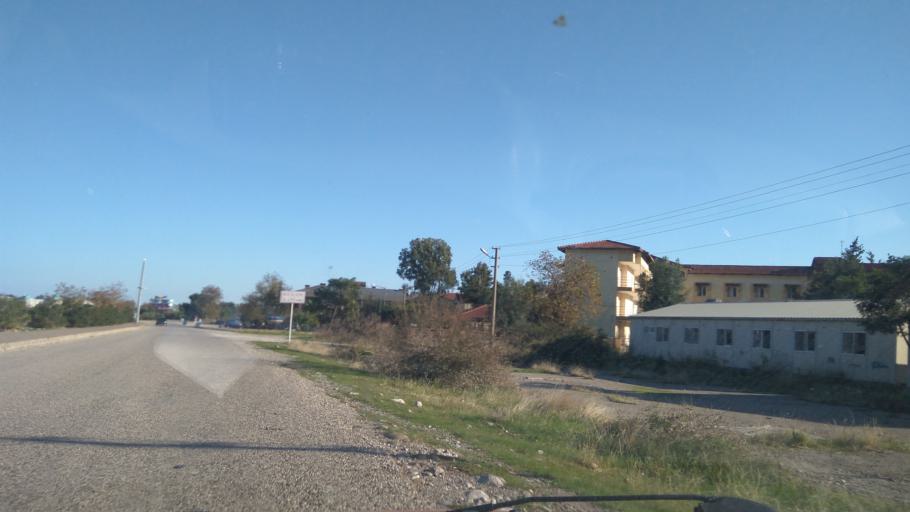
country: TR
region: Antalya
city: Kemer
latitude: 36.5669
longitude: 30.5650
